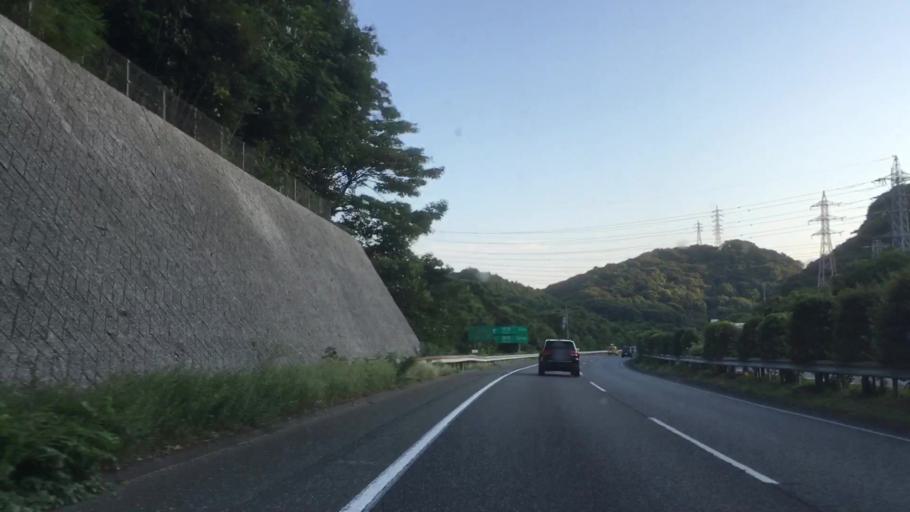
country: JP
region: Yamaguchi
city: Shimonoseki
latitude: 33.8970
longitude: 130.9724
